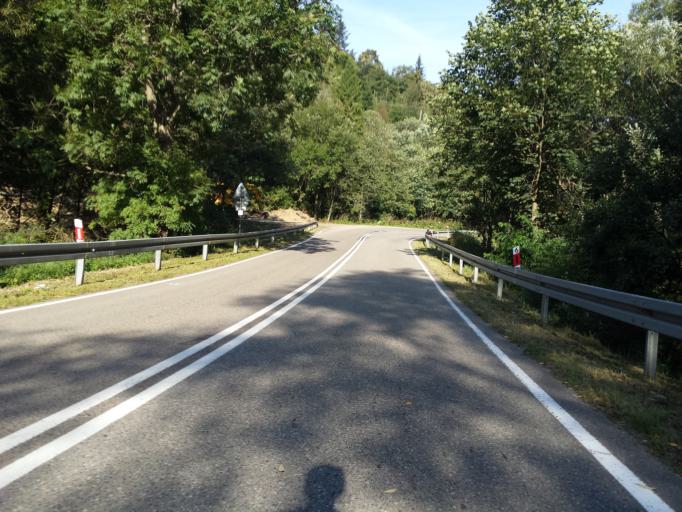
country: PL
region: Subcarpathian Voivodeship
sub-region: Powiat leski
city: Cisna
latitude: 49.2500
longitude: 22.2868
